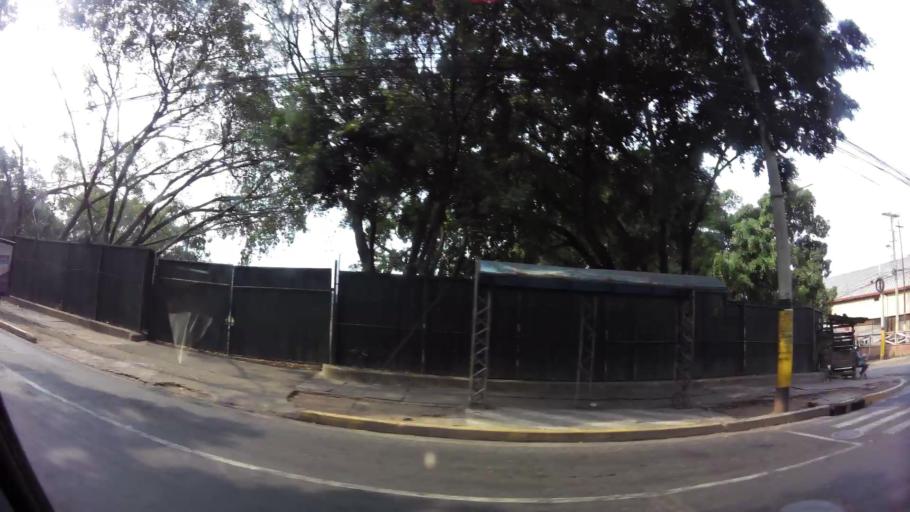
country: HN
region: Francisco Morazan
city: Tegucigalpa
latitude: 14.1029
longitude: -87.1819
